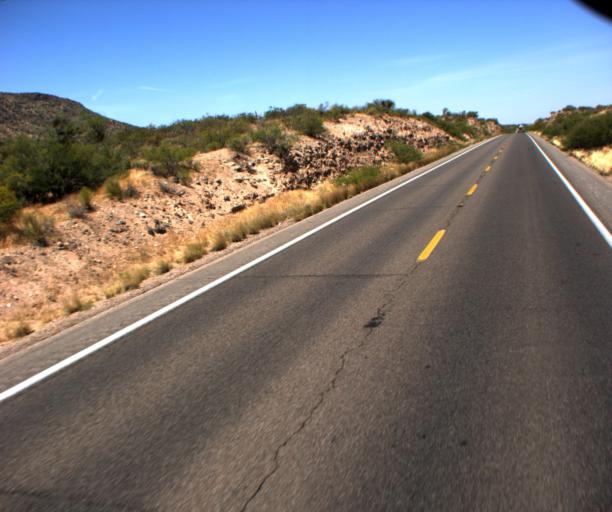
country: US
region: Arizona
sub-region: Gila County
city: Peridot
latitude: 33.3242
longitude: -110.5485
